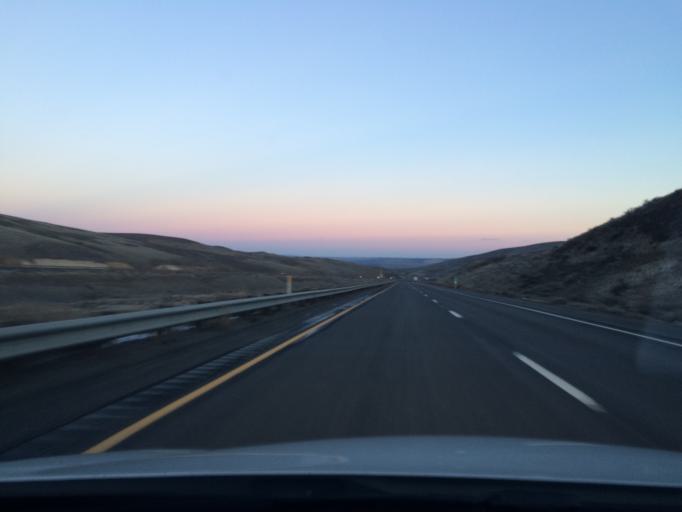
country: US
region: Washington
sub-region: Grant County
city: Mattawa
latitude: 46.9398
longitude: -120.0608
